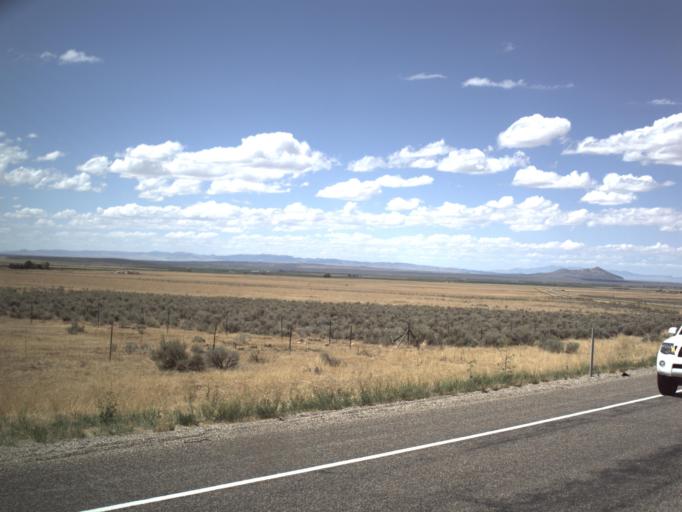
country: US
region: Utah
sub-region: Millard County
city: Fillmore
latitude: 39.1127
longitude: -112.2758
